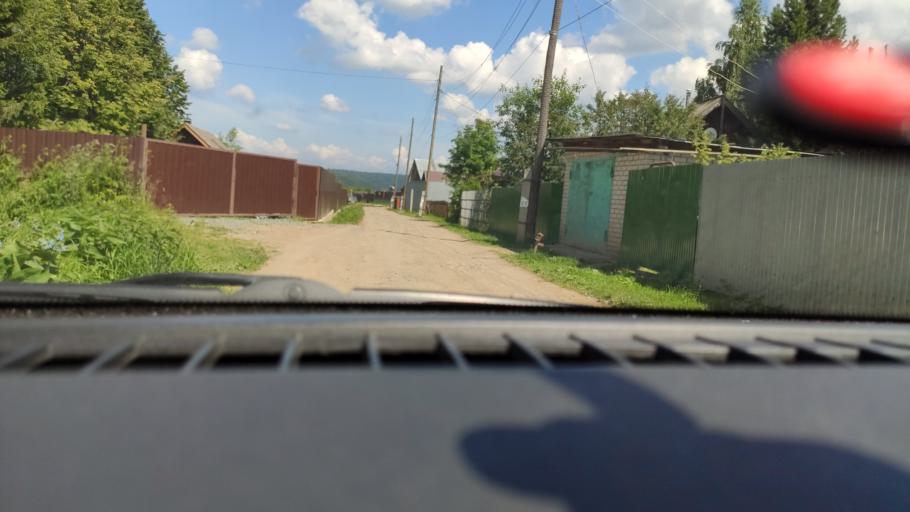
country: RU
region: Perm
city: Sylva
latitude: 58.0469
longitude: 56.7259
